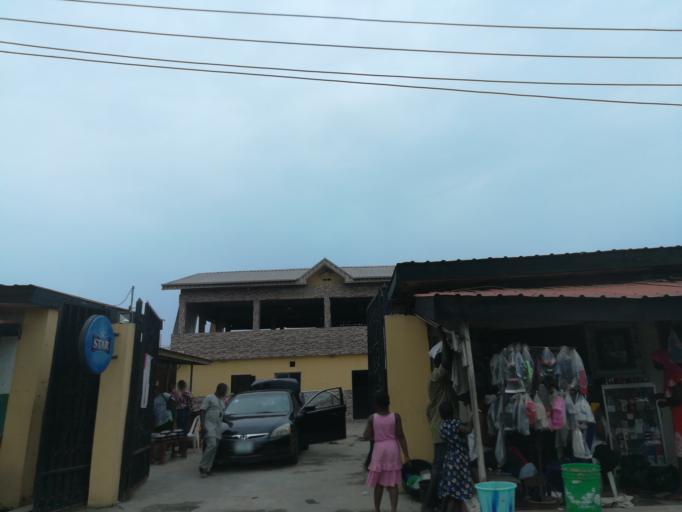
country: NG
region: Lagos
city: Makoko
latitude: 6.4998
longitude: 3.3883
